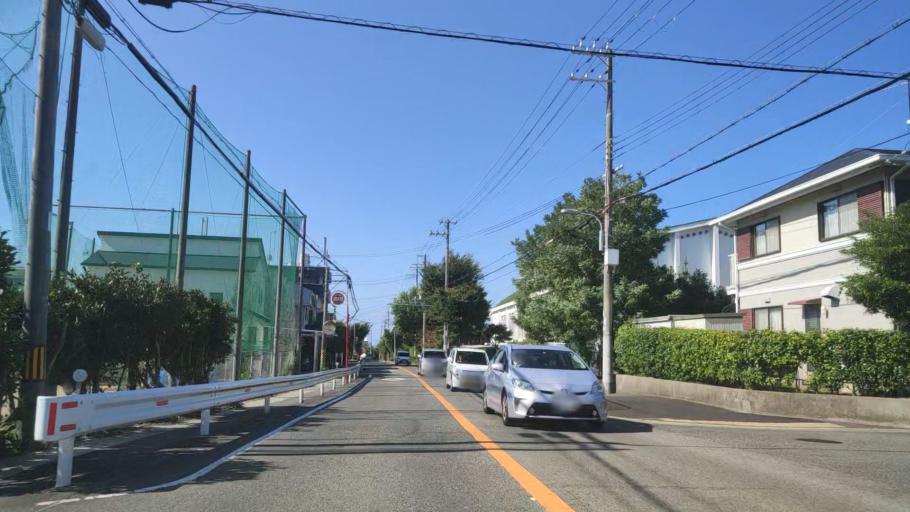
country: JP
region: Hyogo
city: Akashi
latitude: 34.6582
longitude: 135.0100
